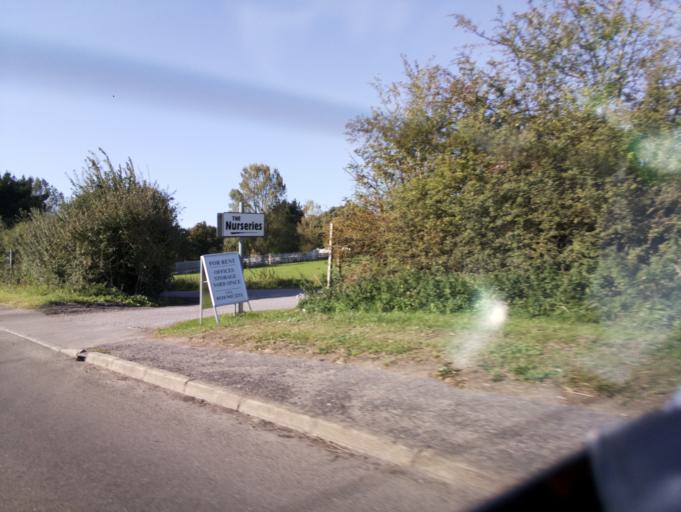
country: GB
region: England
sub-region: West Berkshire
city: Thatcham
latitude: 51.3962
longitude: -1.2022
